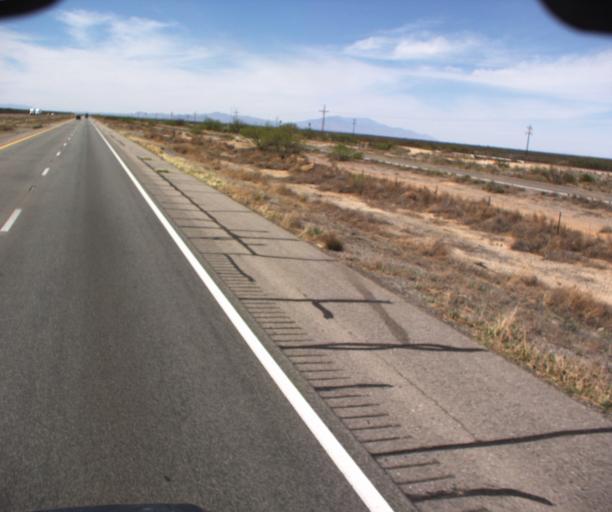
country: US
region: Arizona
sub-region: Cochise County
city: Willcox
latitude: 32.2857
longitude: -109.3026
